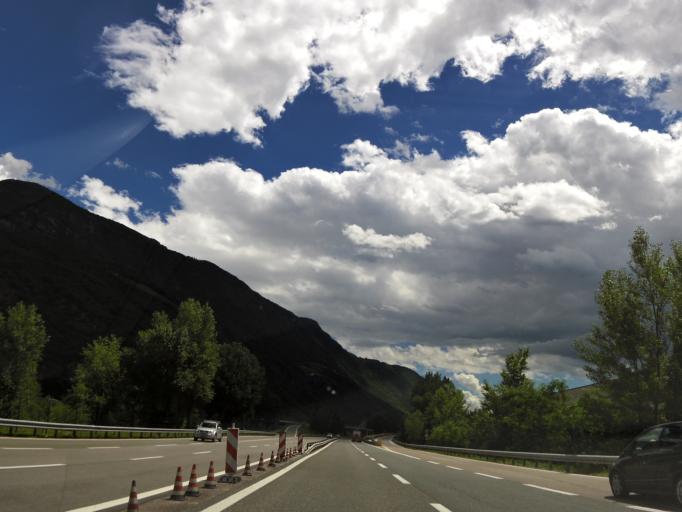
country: IT
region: Trentino-Alto Adige
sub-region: Bolzano
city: Sinigo
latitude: 46.6324
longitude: 11.1741
